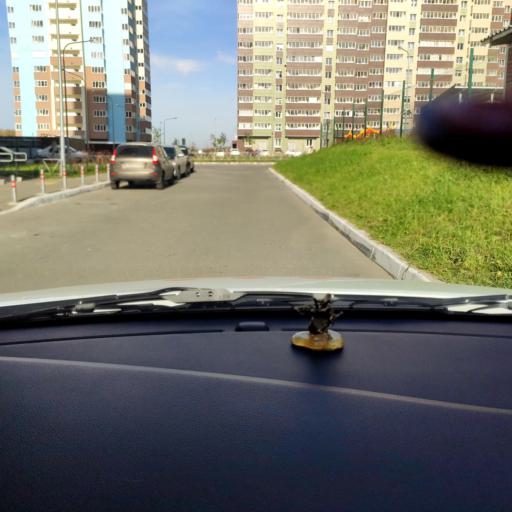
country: RU
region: Tatarstan
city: Osinovo
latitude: 55.8651
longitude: 48.8742
